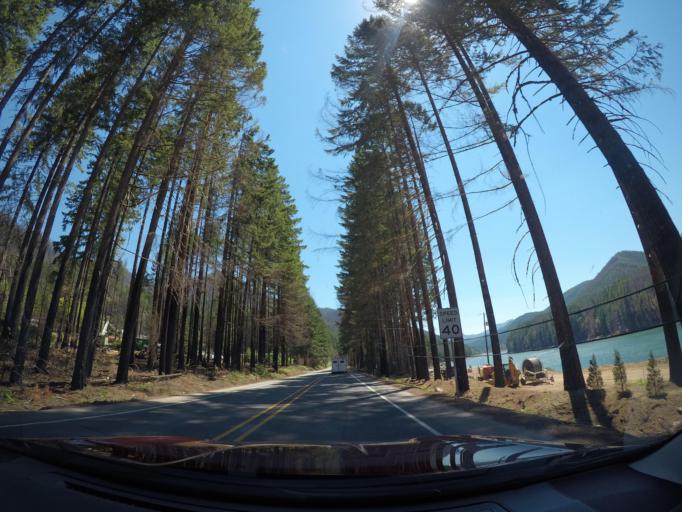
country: US
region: Oregon
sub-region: Linn County
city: Mill City
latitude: 44.7293
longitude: -122.1449
